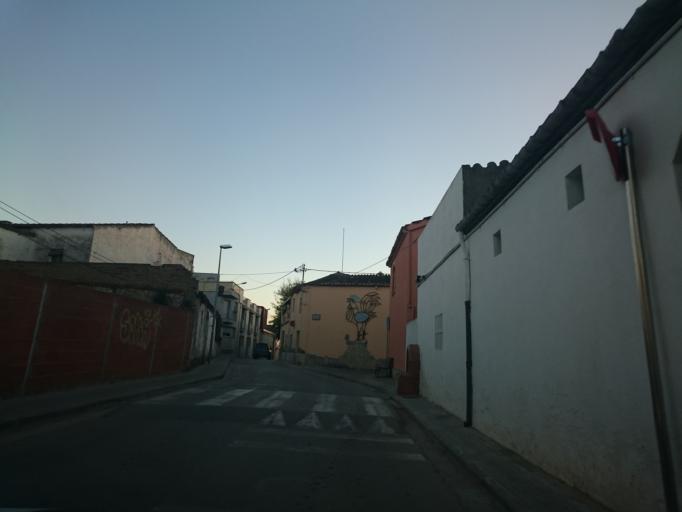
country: ES
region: Catalonia
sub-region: Provincia de Barcelona
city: La Granada
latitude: 41.3488
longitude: 1.7382
